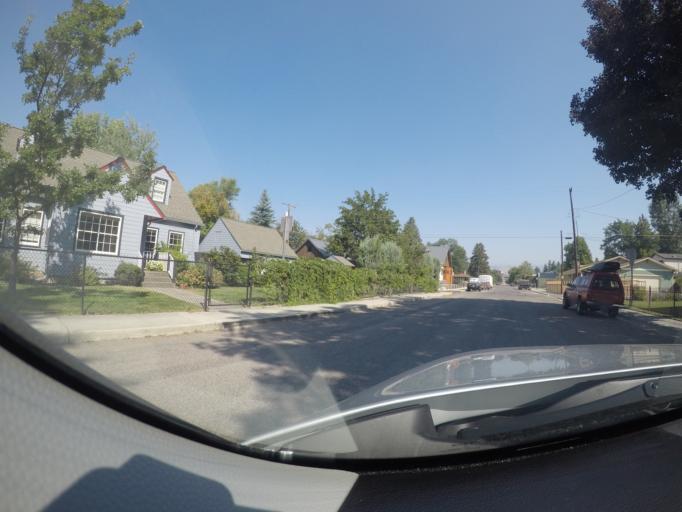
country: US
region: Montana
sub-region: Missoula County
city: Missoula
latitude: 46.8534
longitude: -113.9854
